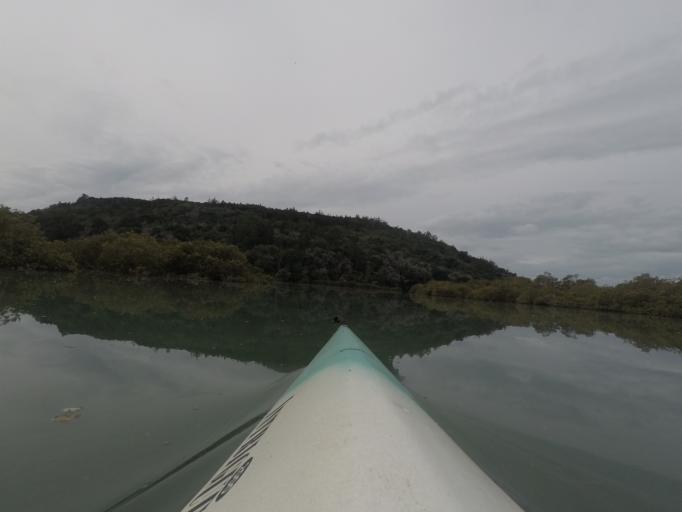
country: NZ
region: Auckland
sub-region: Auckland
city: Rothesay Bay
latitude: -36.6758
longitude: 174.7095
